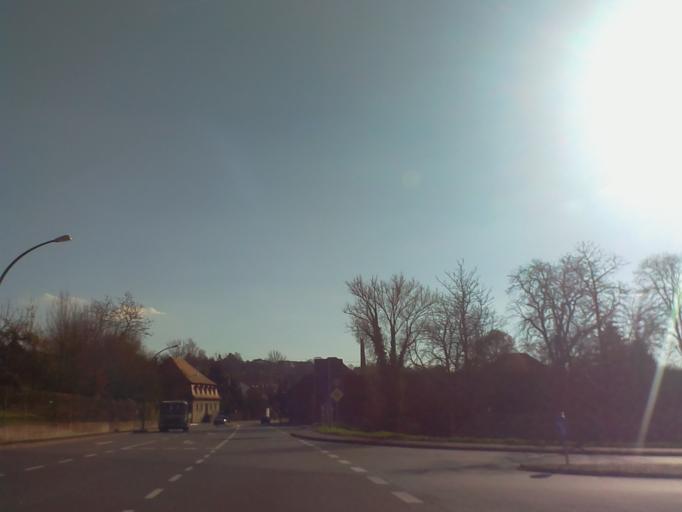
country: DE
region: Bavaria
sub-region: Regierungsbezirk Unterfranken
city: Bad Kissingen
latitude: 50.2190
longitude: 10.0709
